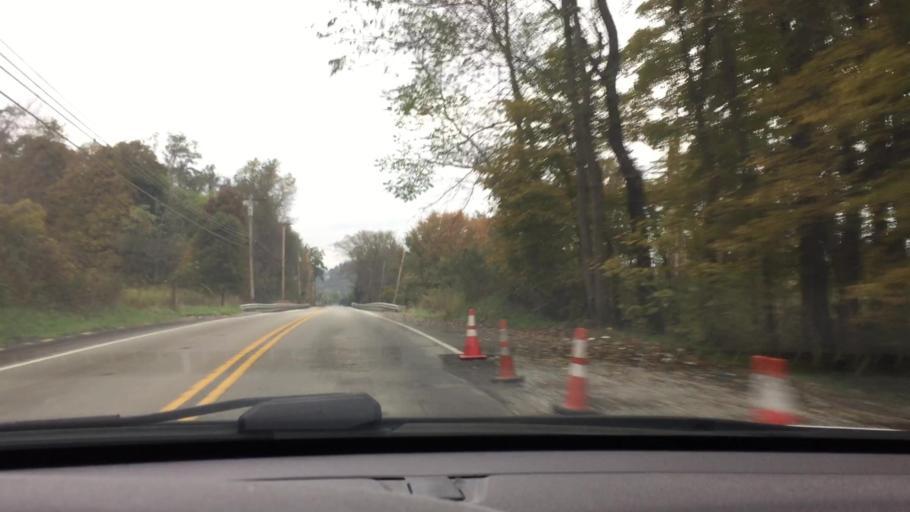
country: US
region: Pennsylvania
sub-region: Fayette County
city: Fairhope
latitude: 40.0910
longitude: -79.8454
